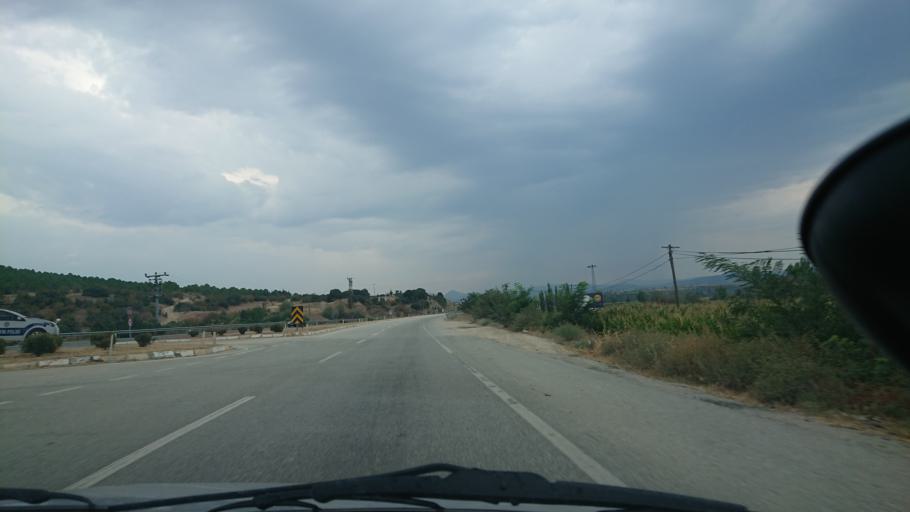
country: TR
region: Manisa
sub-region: Kula
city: Kula
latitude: 38.5901
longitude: 28.8089
